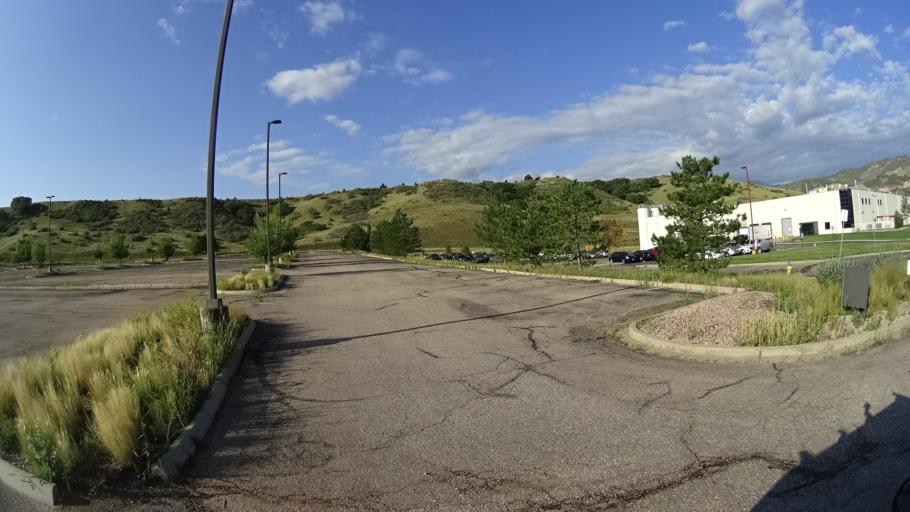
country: US
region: Colorado
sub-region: El Paso County
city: Manitou Springs
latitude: 38.8936
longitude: -104.8618
